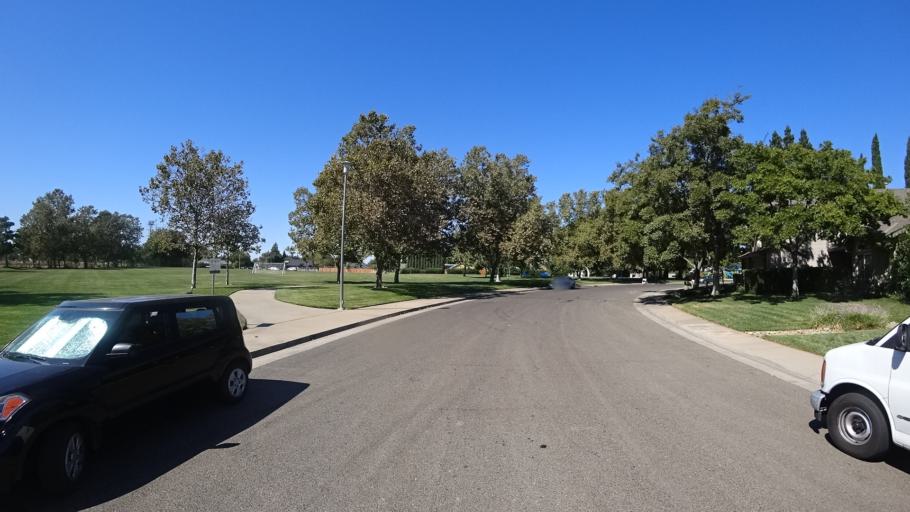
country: US
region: California
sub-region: Sacramento County
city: Laguna
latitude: 38.4273
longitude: -121.4408
